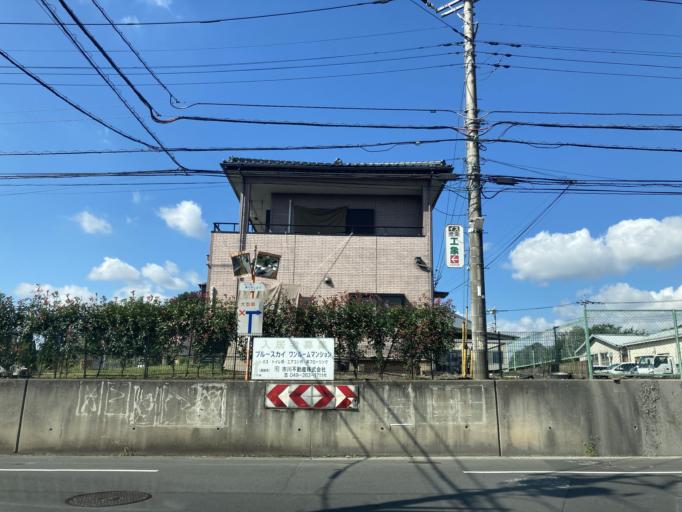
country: JP
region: Saitama
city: Tokorozawa
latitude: 35.8102
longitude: 139.5004
